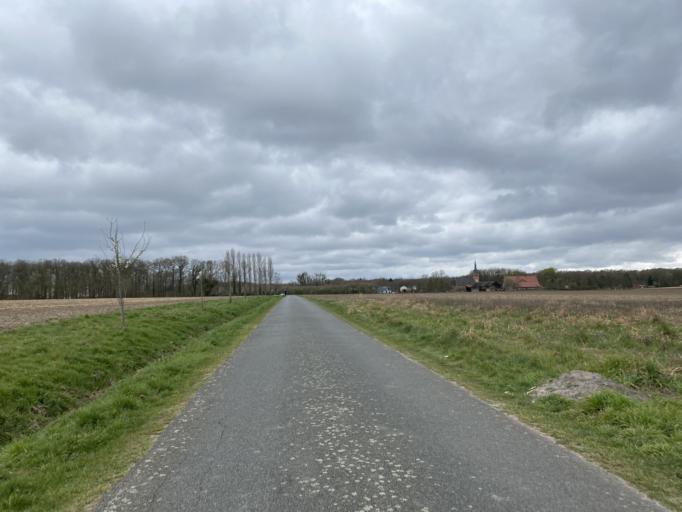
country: DE
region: North Rhine-Westphalia
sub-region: Regierungsbezirk Arnsberg
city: Welver
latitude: 51.6818
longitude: 7.9238
